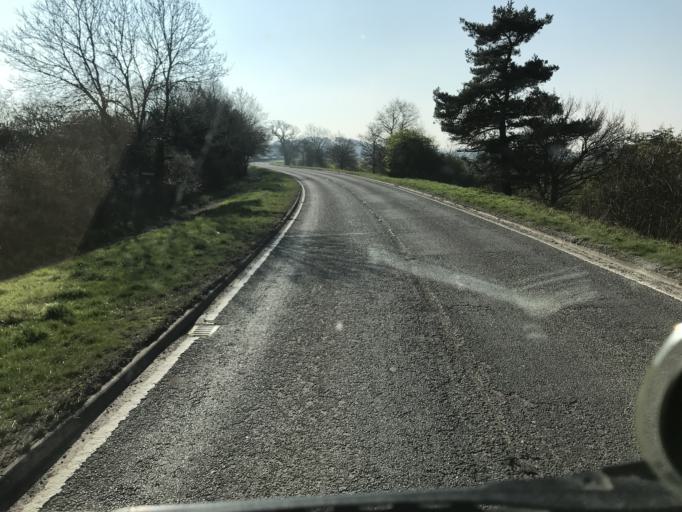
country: GB
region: England
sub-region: Cheshire West and Chester
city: Waverton
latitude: 53.1621
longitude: -2.8164
